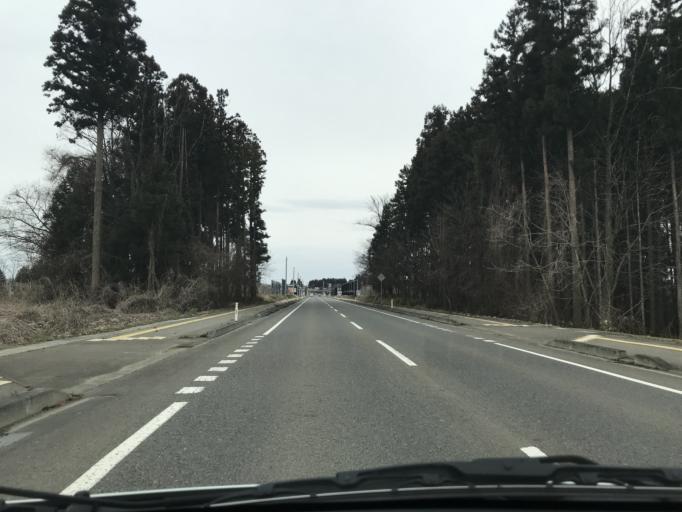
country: JP
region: Iwate
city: Hanamaki
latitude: 39.3637
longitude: 141.1108
